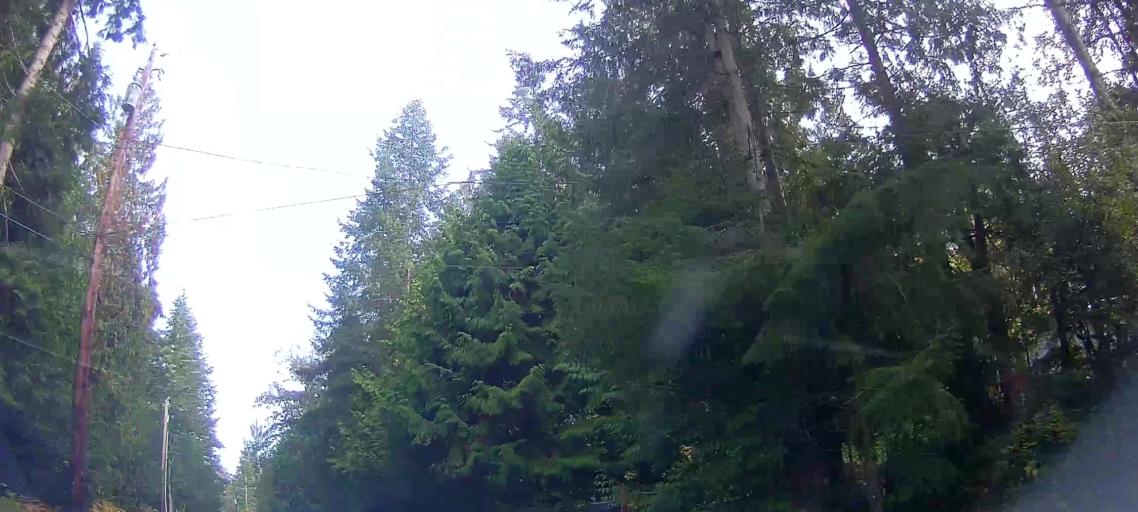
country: US
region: Washington
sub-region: Snohomish County
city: Stanwood
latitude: 48.2808
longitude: -122.3487
